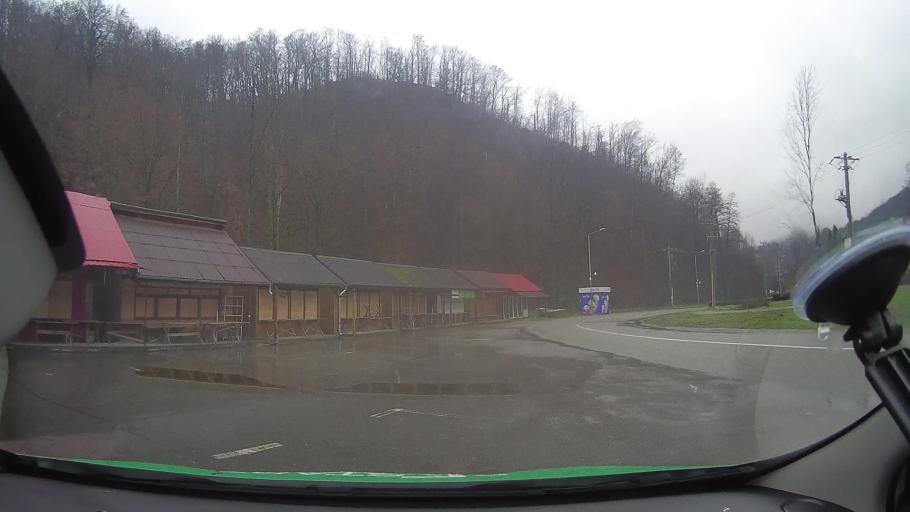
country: RO
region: Arad
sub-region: Comuna Moneasa
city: Moneasa
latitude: 46.4626
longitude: 22.2608
